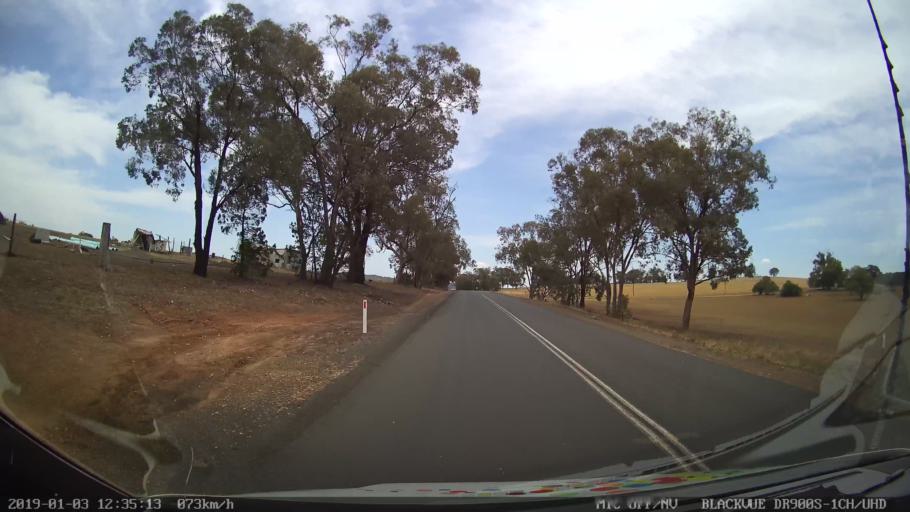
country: AU
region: New South Wales
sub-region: Weddin
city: Grenfell
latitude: -33.8689
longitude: 148.1692
